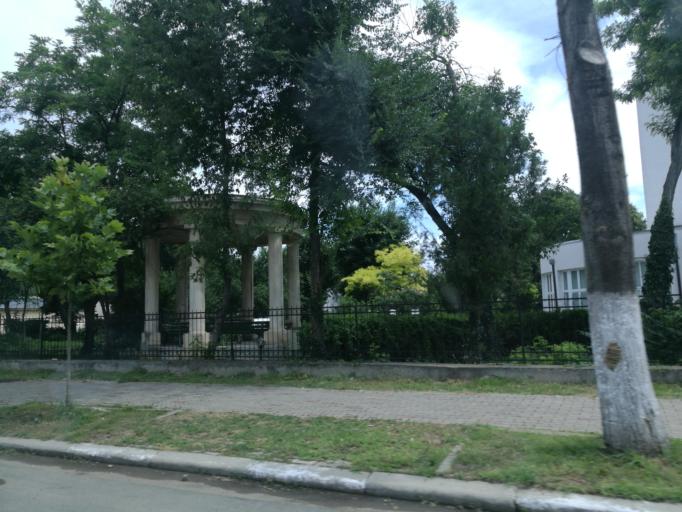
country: RO
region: Constanta
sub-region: Oras Eforie
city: Eforie Nord
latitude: 44.0683
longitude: 28.6327
